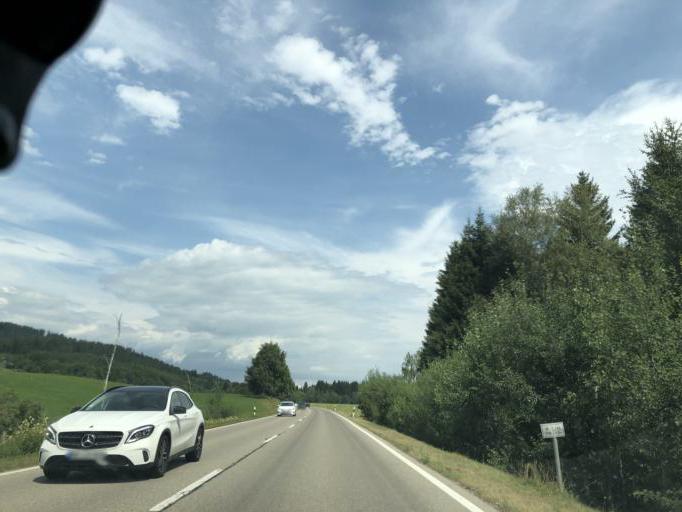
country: DE
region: Bavaria
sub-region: Swabia
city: Wertach
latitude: 47.6085
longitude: 10.4289
